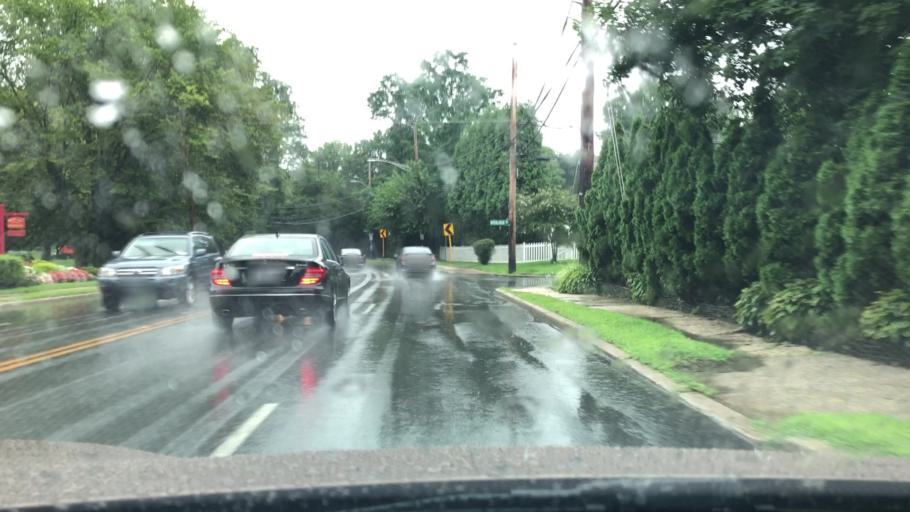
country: US
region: New York
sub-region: Westchester County
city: Tuckahoe
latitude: 40.9555
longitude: -73.8047
